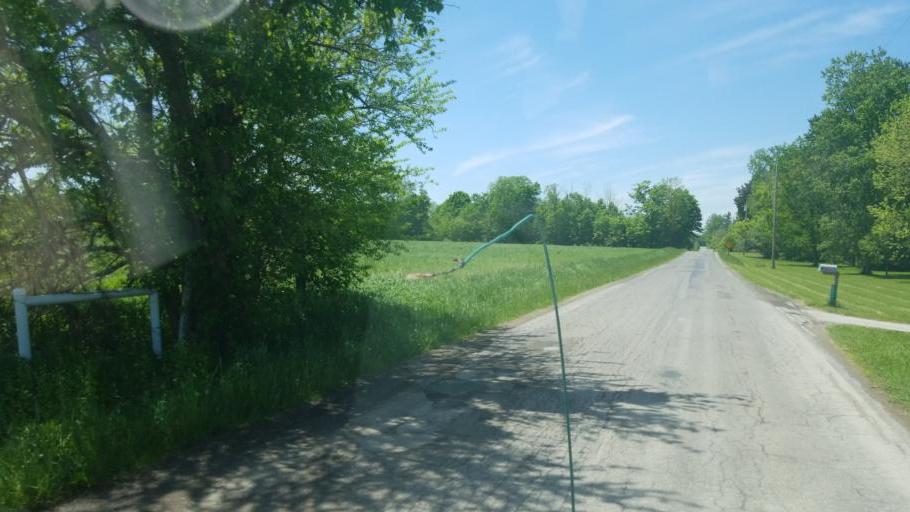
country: US
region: Ohio
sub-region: Huron County
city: Greenwich
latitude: 40.9680
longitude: -82.4220
